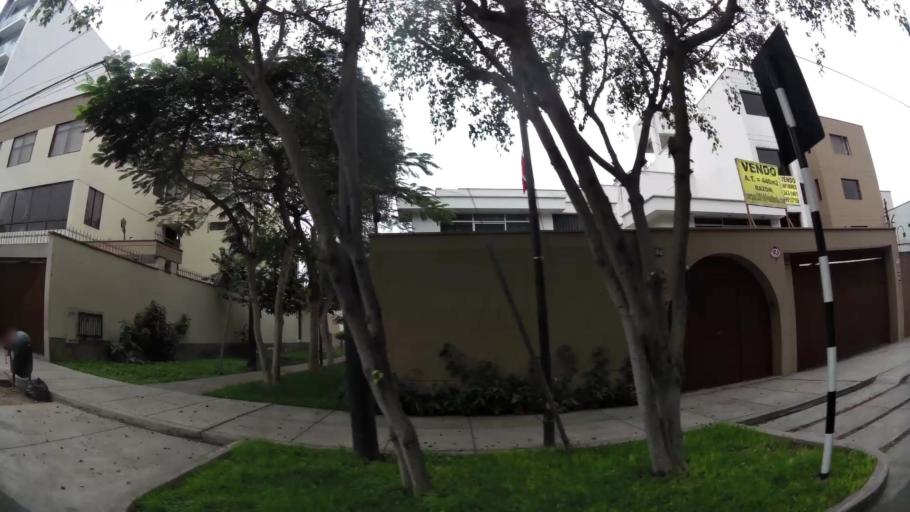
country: PE
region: Lima
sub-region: Lima
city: San Luis
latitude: -12.0927
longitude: -77.0160
